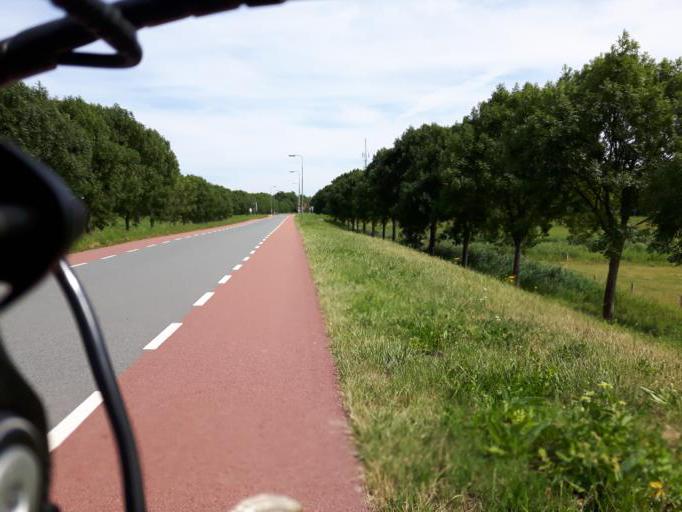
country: NL
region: North Brabant
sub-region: Gemeente Steenbergen
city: Nieuw-Vossemeer
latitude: 51.5833
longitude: 4.2161
